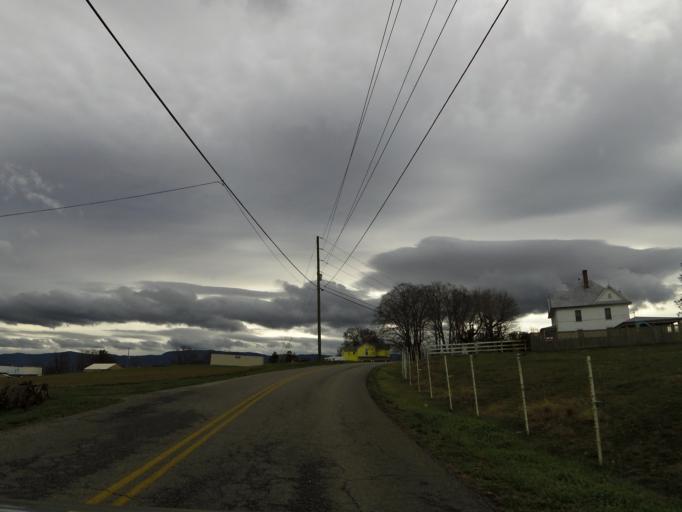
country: US
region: Tennessee
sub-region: Greene County
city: Tusculum
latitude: 36.1970
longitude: -82.7388
